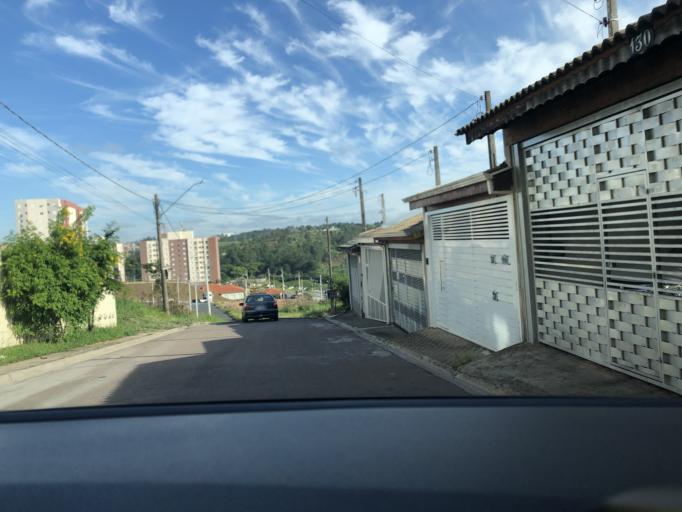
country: BR
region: Sao Paulo
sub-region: Campo Limpo Paulista
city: Campo Limpo Paulista
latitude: -23.2135
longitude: -46.8042
